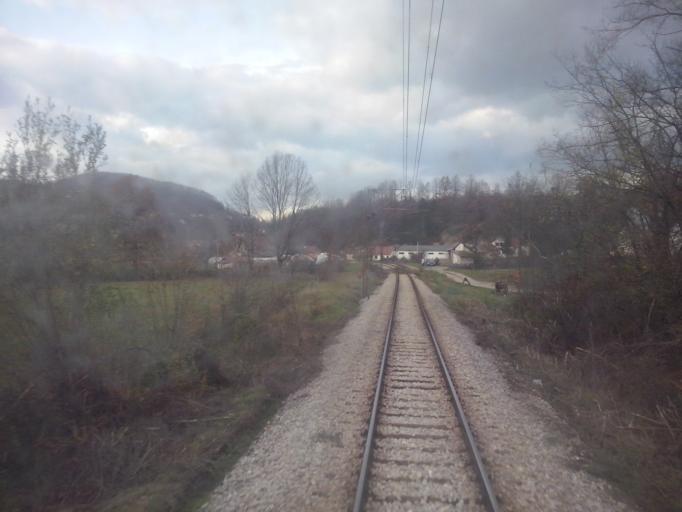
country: RS
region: Central Serbia
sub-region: Zlatiborski Okrug
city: Kosjeric
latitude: 43.9716
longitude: 19.9539
